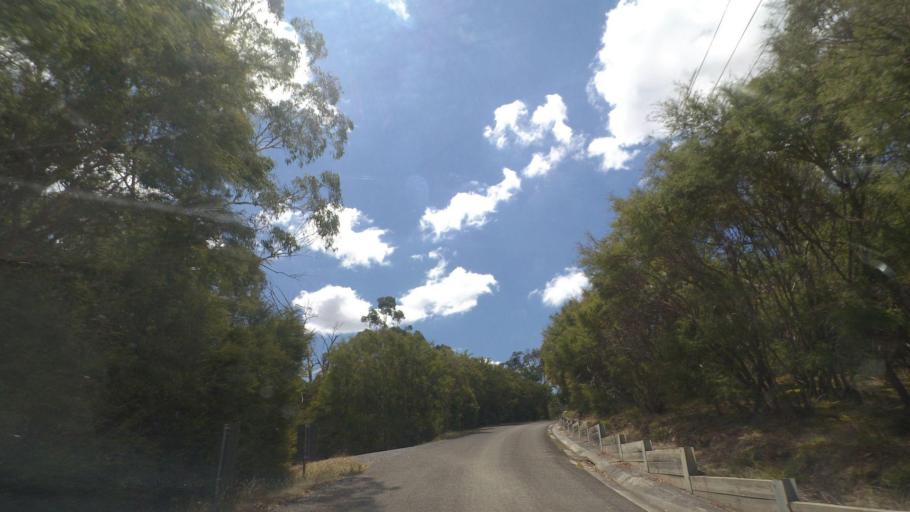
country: AU
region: Victoria
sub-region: Yarra Ranges
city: Chirnside Park
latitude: -37.7202
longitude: 145.2782
